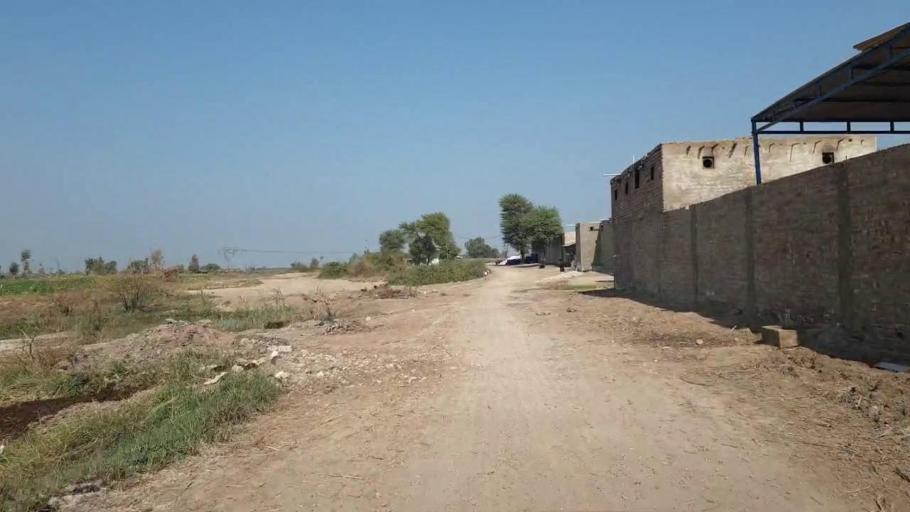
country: PK
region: Sindh
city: Hala
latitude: 25.9534
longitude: 68.4271
